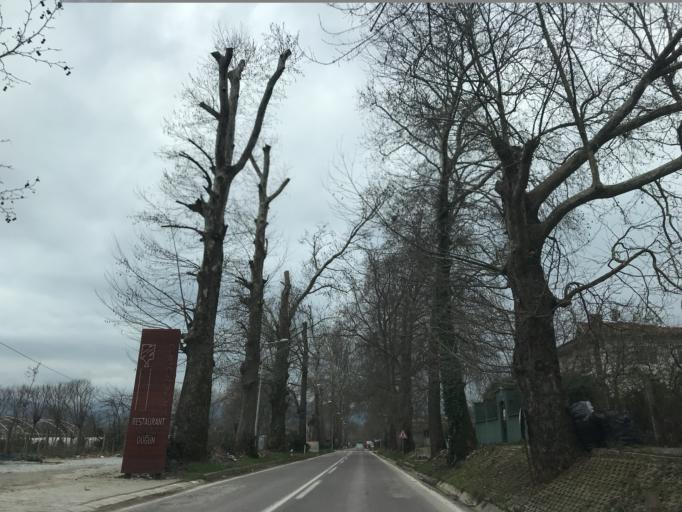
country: TR
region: Yalova
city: Kadikoy
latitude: 40.6420
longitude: 29.2289
